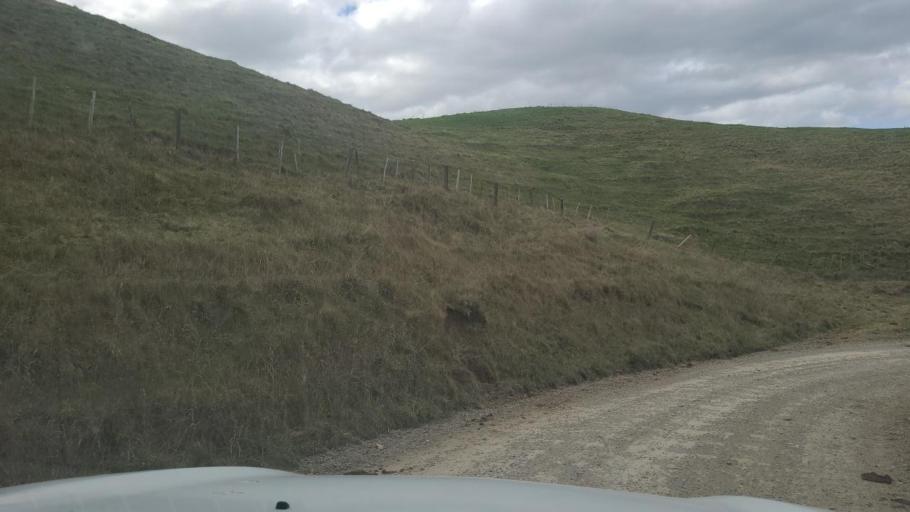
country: NZ
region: Hawke's Bay
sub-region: Hastings District
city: Hastings
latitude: -39.7512
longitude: 176.6911
